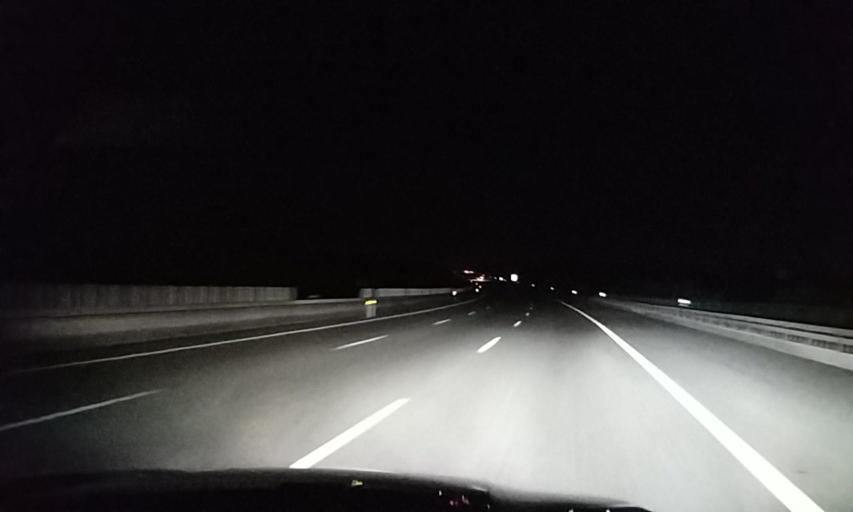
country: PT
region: Santarem
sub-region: Santarem
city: Santarem
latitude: 39.2841
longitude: -8.6917
